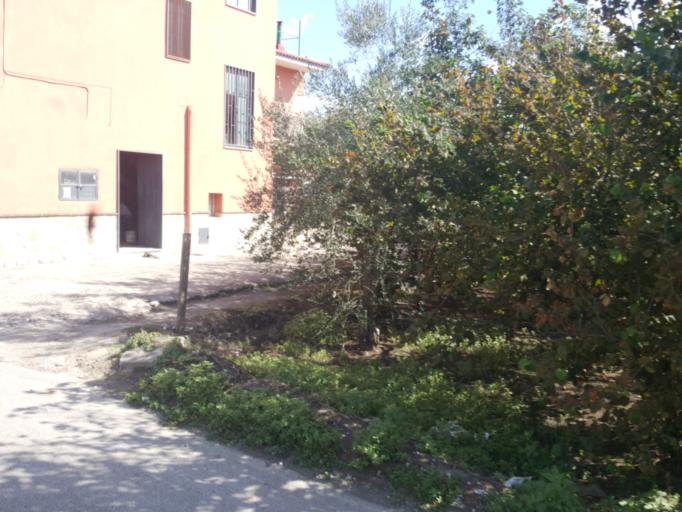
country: IT
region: Campania
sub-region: Provincia di Napoli
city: Piazzolla
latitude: 40.9050
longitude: 14.5289
